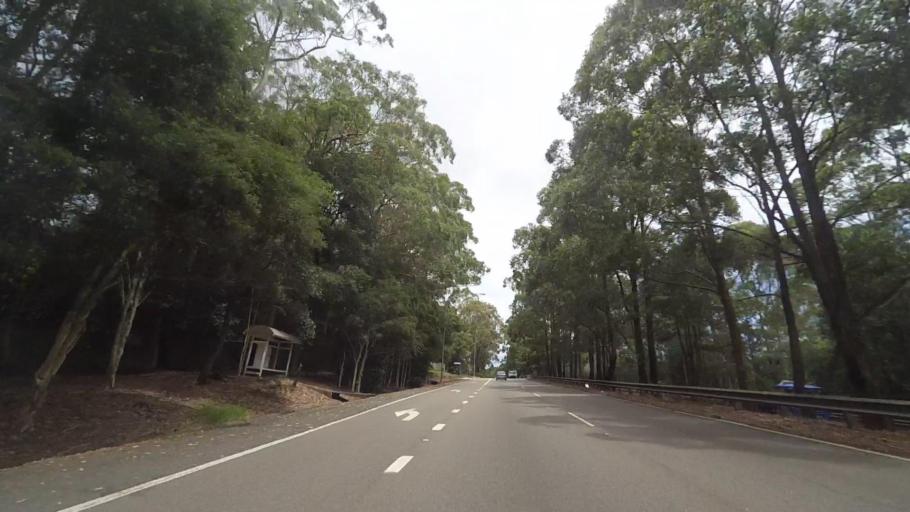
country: AU
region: New South Wales
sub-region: Wyong Shire
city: Berkeley Vale
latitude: -33.3477
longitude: 151.4310
